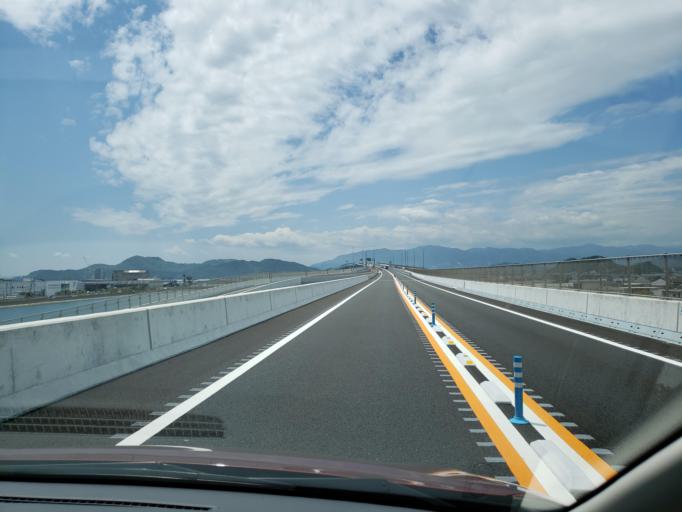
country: JP
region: Tokushima
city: Tokushima-shi
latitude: 34.0625
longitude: 134.5926
